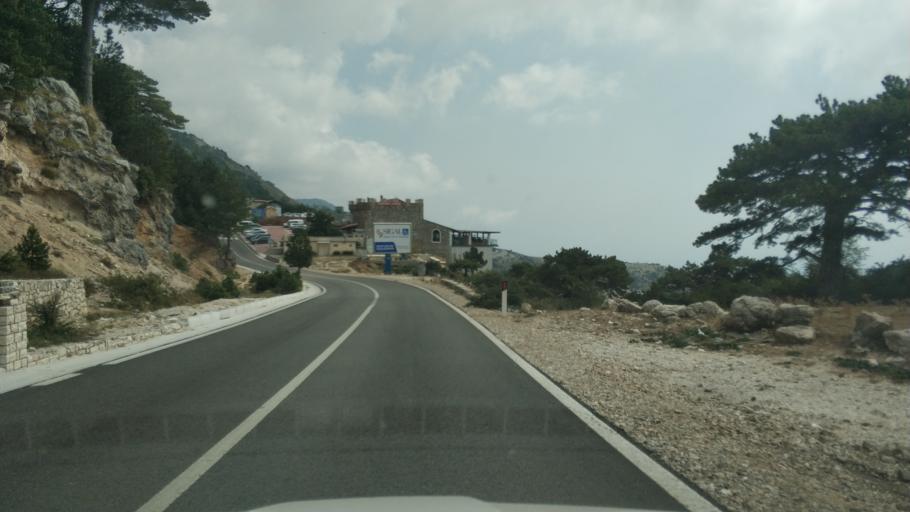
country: AL
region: Vlore
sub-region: Rrethi i Vlores
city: Vranisht
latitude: 40.1975
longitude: 19.5935
